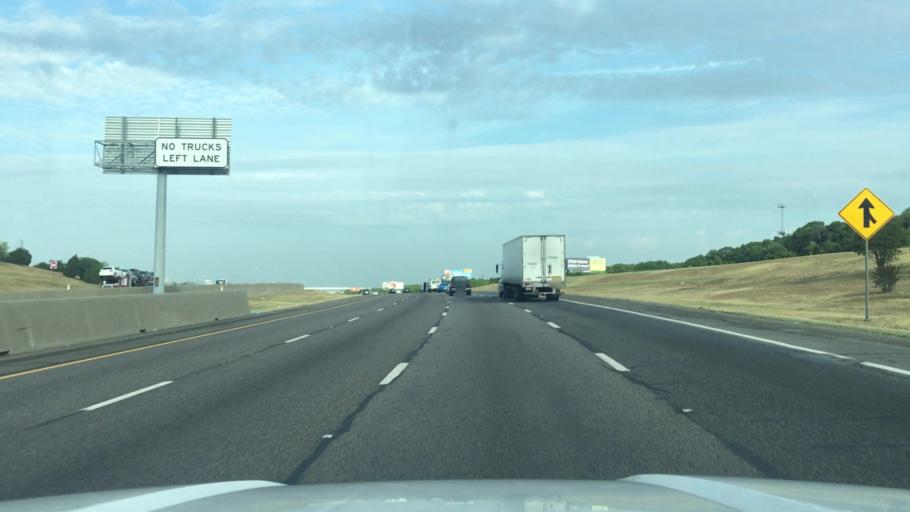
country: US
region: Texas
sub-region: Dallas County
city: Duncanville
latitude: 32.6700
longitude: -96.9266
